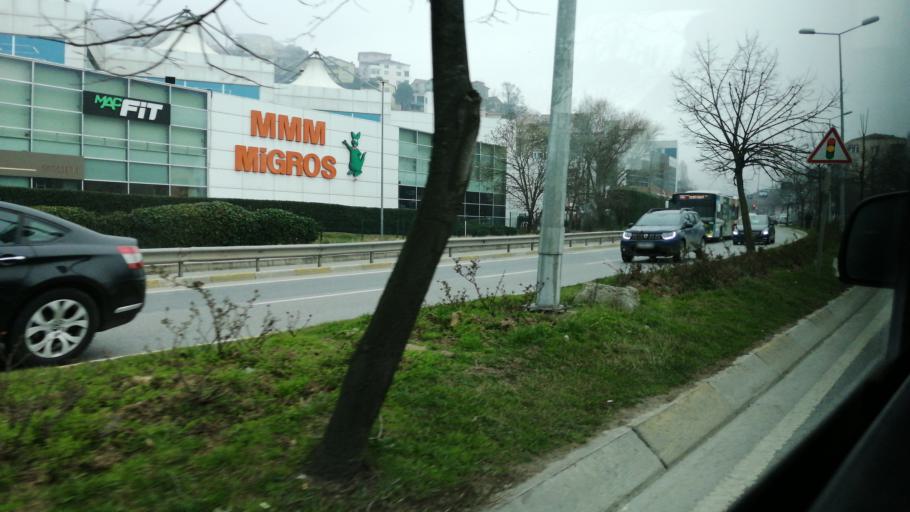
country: TR
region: Istanbul
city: Umraniye
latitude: 41.0803
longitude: 29.0789
